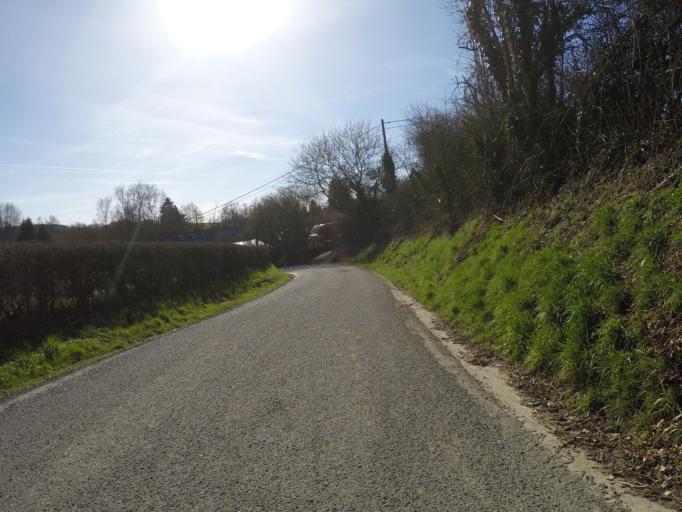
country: BE
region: Wallonia
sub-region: Province de Namur
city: Gesves
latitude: 50.3596
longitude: 5.0858
